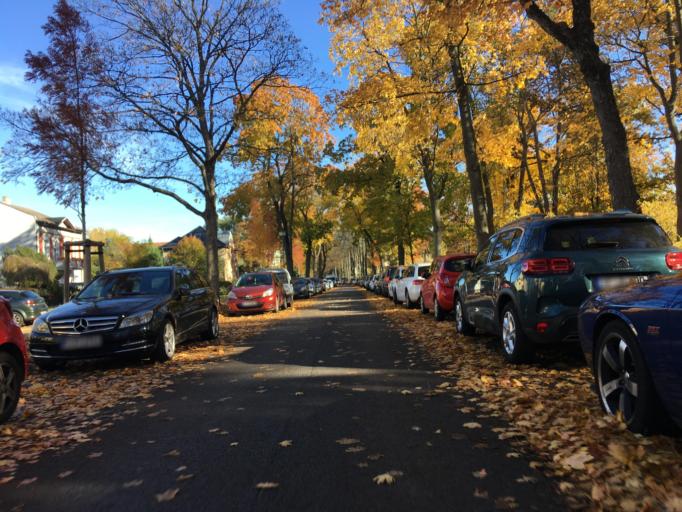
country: DE
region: Berlin
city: Friedrichshagen
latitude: 52.4560
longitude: 13.6295
